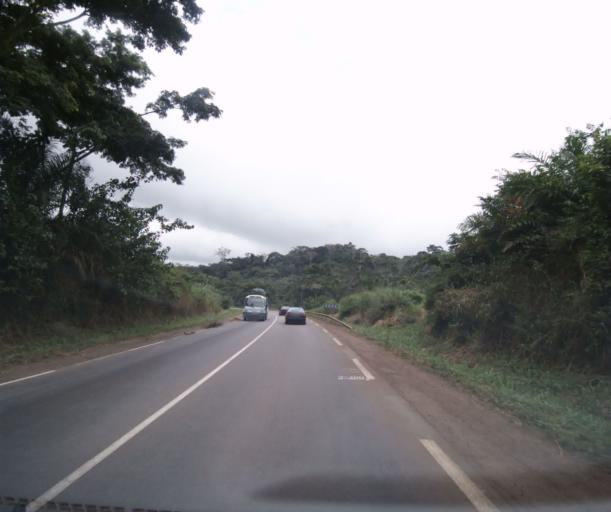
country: CM
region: Centre
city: Mbankomo
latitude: 3.7817
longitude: 11.2440
